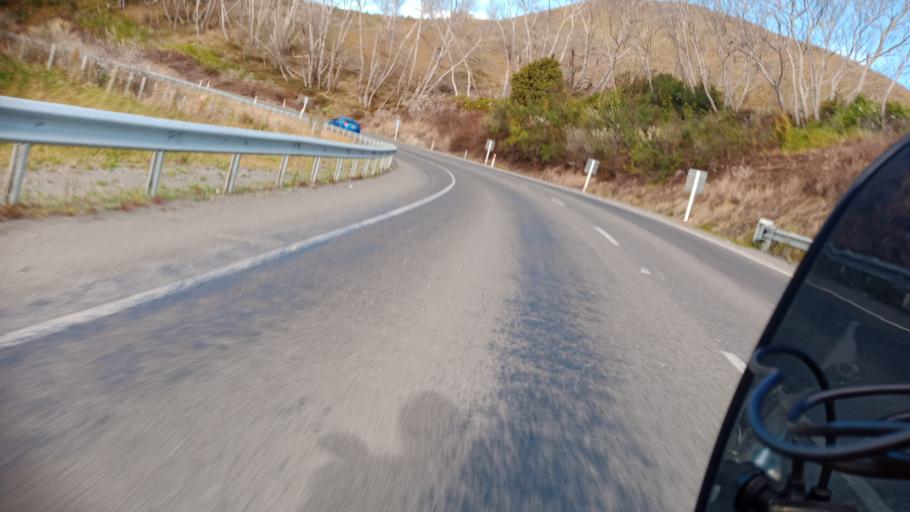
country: NZ
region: Gisborne
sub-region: Gisborne District
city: Gisborne
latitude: -38.8238
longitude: 177.9036
